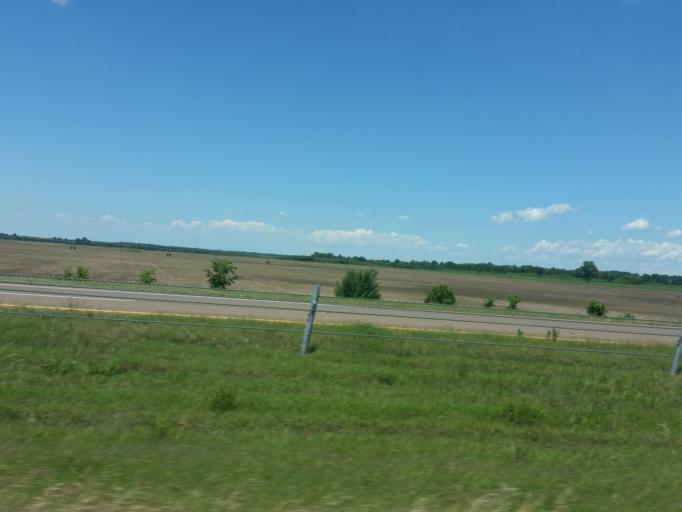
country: US
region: Missouri
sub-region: Pemiscot County
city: Caruthersville
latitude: 36.0873
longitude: -89.5592
